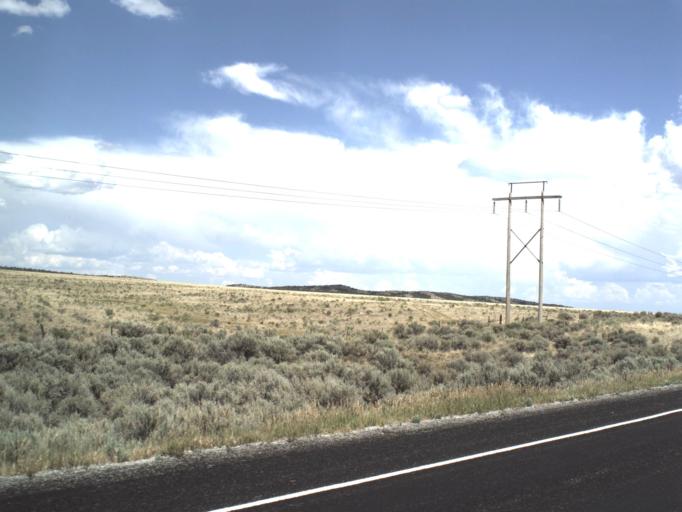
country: US
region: Idaho
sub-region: Minidoka County
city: Rupert
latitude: 41.9961
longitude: -113.1913
